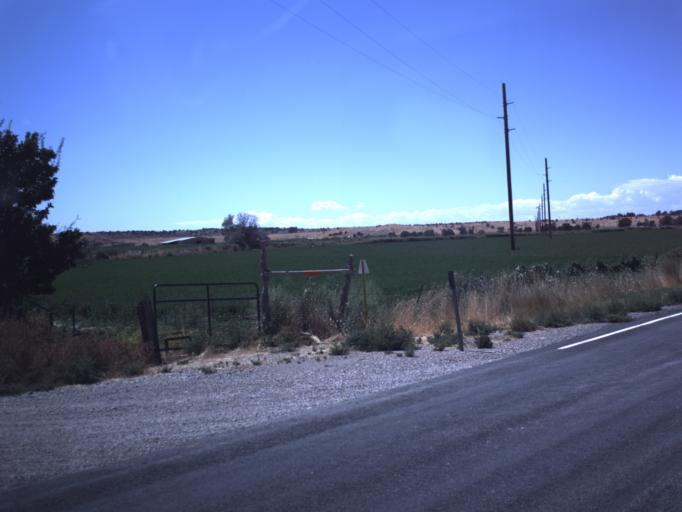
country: US
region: Utah
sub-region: Millard County
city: Delta
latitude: 39.5378
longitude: -112.2593
